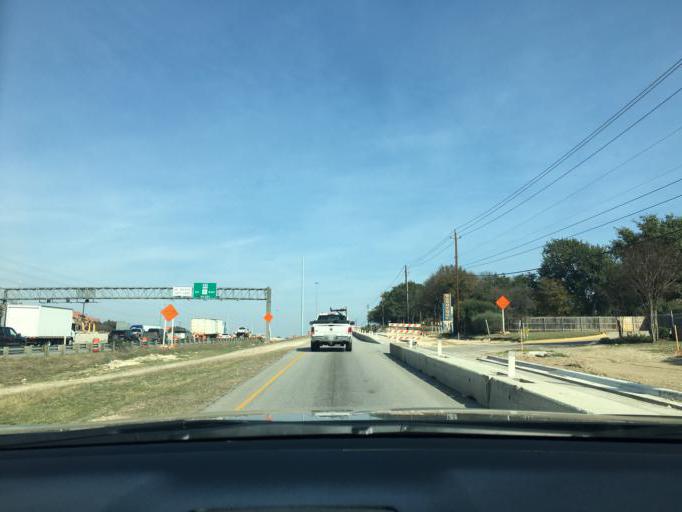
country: US
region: Texas
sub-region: Travis County
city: Onion Creek
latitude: 30.1806
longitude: -97.7767
